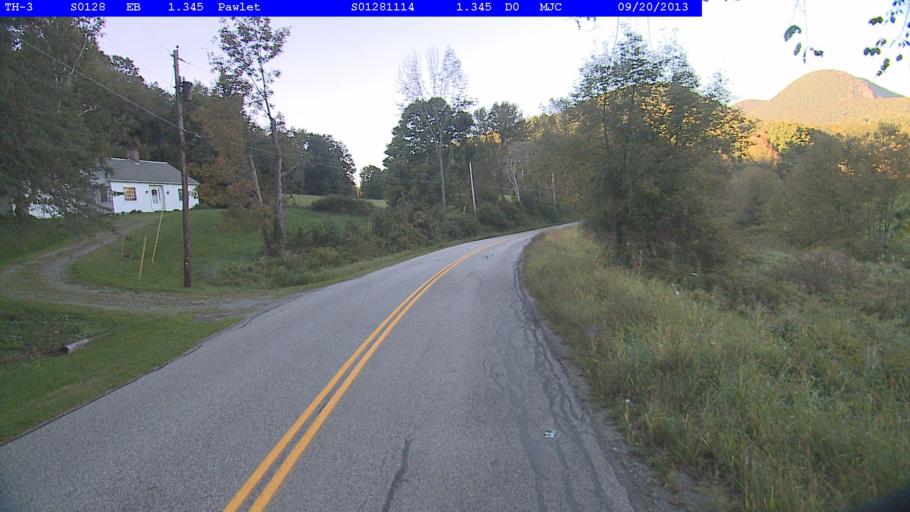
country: US
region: New York
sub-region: Washington County
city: Granville
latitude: 43.3738
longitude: -73.2066
